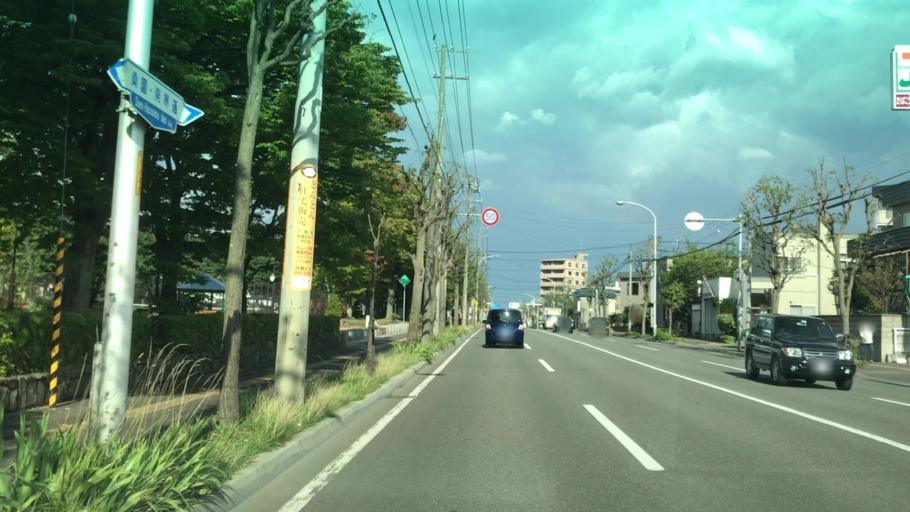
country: JP
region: Hokkaido
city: Sapporo
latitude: 43.0849
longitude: 141.2981
